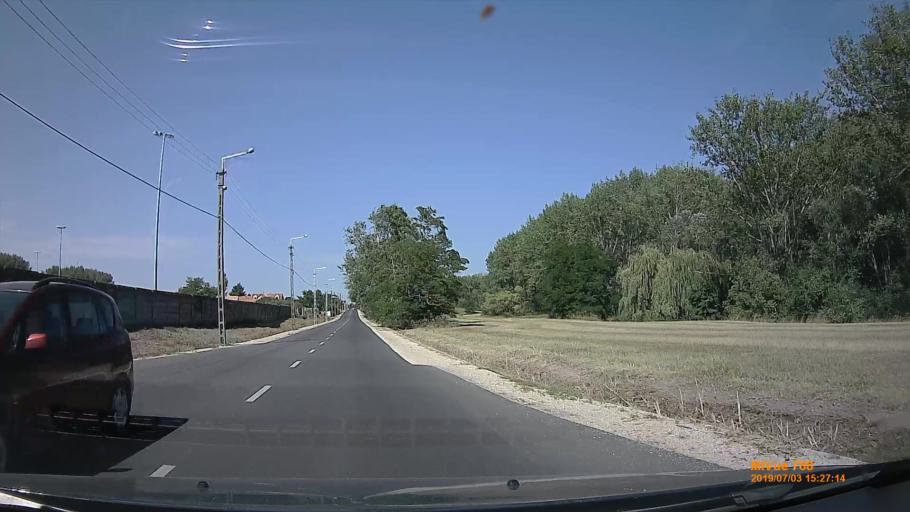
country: HU
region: Gyor-Moson-Sopron
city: Gyor
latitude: 47.7187
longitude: 17.6562
